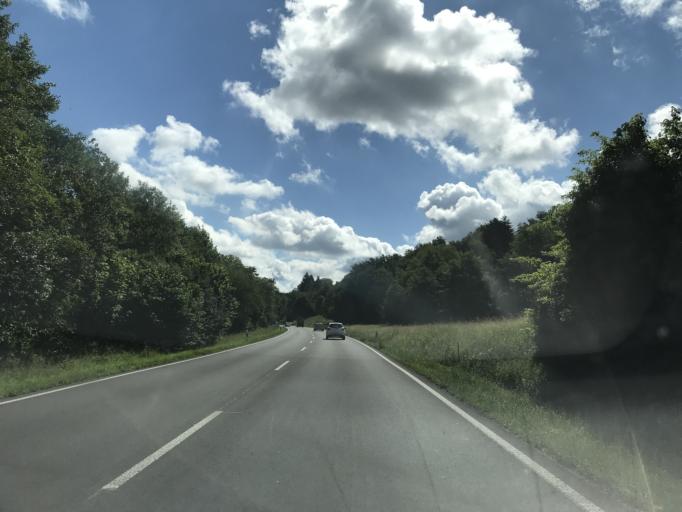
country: DE
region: Baden-Wuerttemberg
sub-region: Freiburg Region
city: Schopfheim
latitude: 47.6411
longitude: 7.8096
